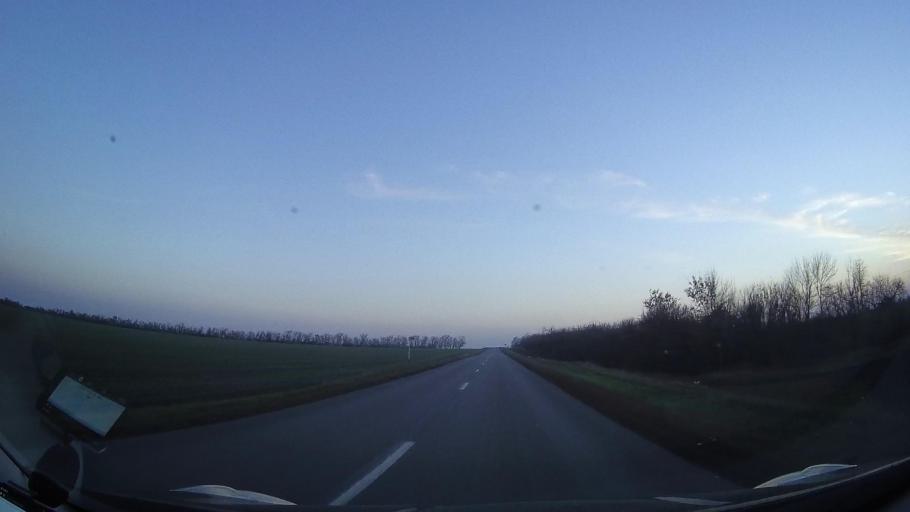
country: RU
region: Rostov
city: Zernograd
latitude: 46.9160
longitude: 40.3388
